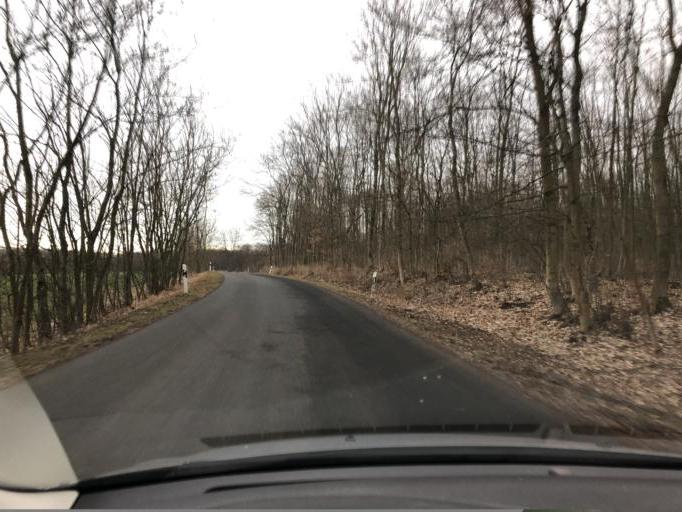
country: DE
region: Thuringia
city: Ramsla
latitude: 51.0335
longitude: 11.2589
